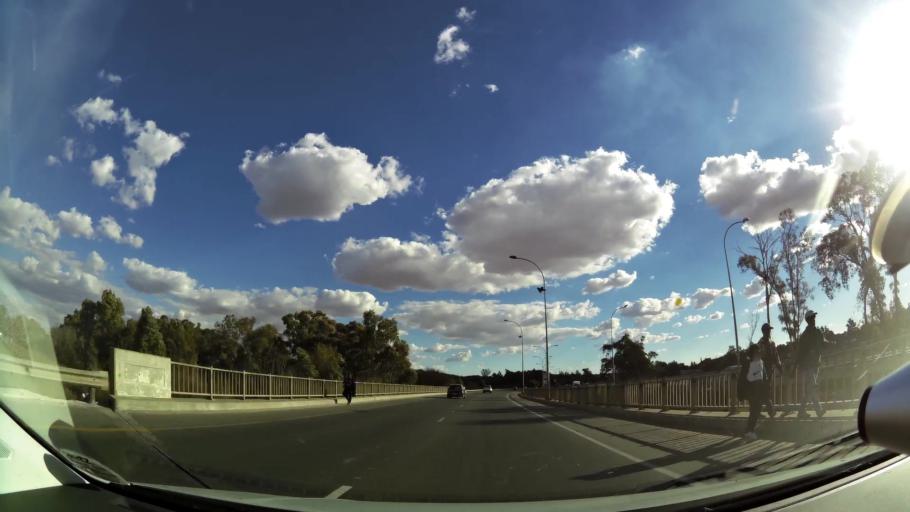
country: ZA
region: North-West
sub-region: Dr Kenneth Kaunda District Municipality
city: Klerksdorp
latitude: -26.8637
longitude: 26.6588
